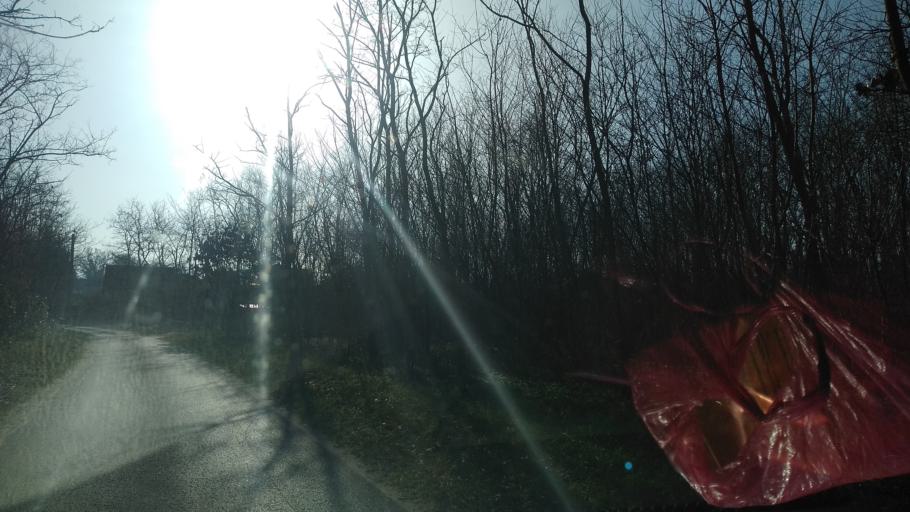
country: HU
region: Somogy
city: Barcs
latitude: 45.9551
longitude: 17.5078
